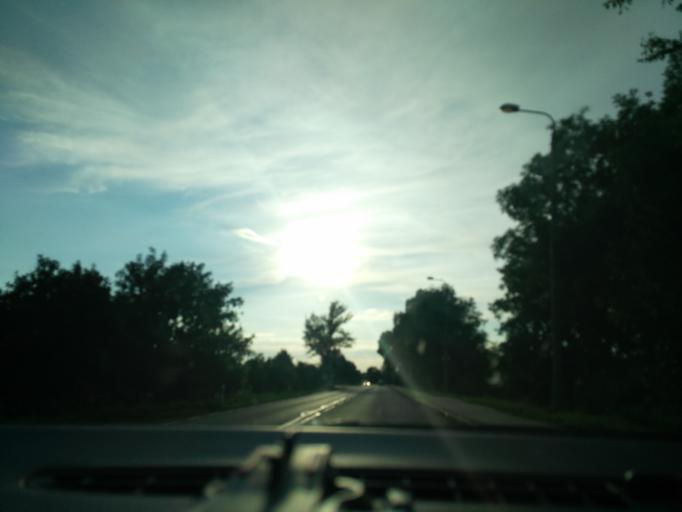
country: PL
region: Lublin Voivodeship
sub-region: Powiat krasnicki
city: Krasnik
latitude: 50.9090
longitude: 22.2625
